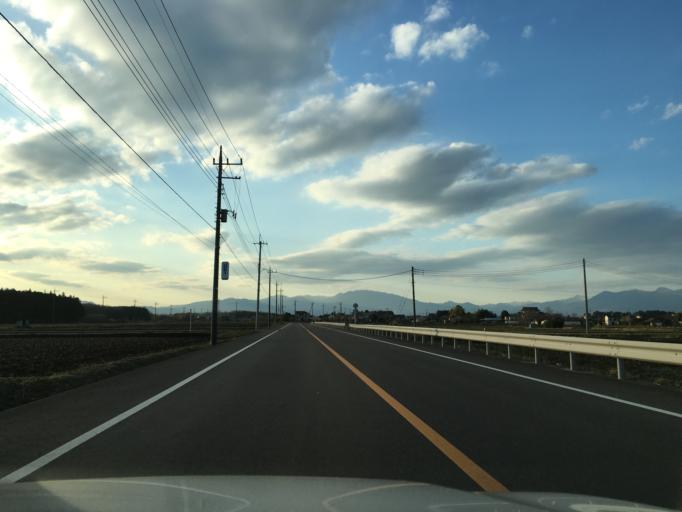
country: JP
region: Tochigi
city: Otawara
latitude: 36.8764
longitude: 140.0704
